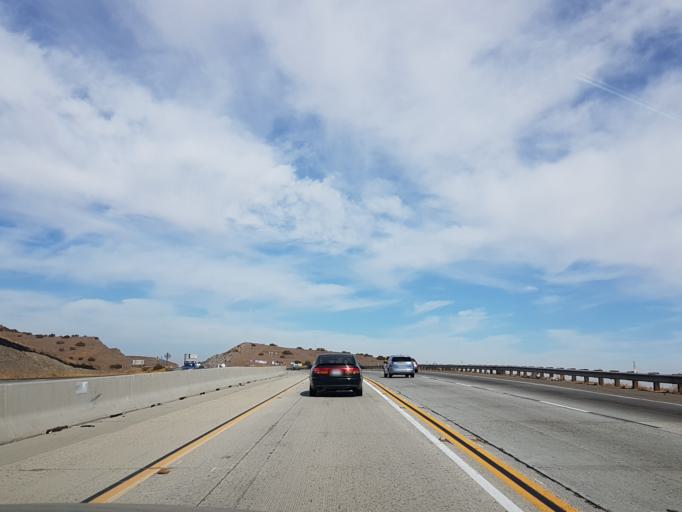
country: US
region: California
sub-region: Los Angeles County
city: Vincent
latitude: 34.5203
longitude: -118.1107
